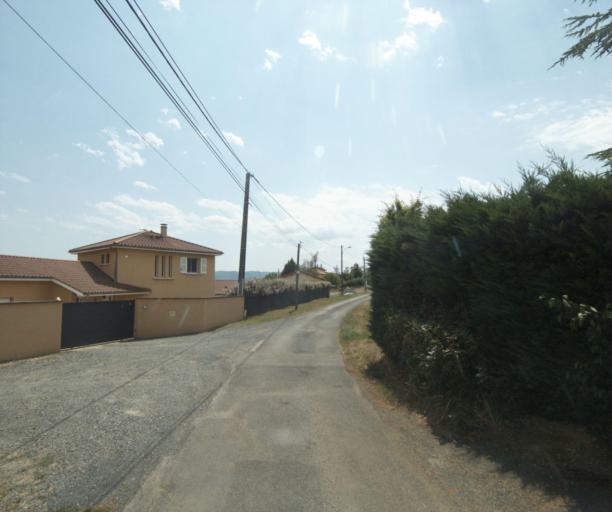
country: FR
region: Rhone-Alpes
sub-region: Departement du Rhone
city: Saint-Germain-Nuelles
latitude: 45.8615
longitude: 4.6095
